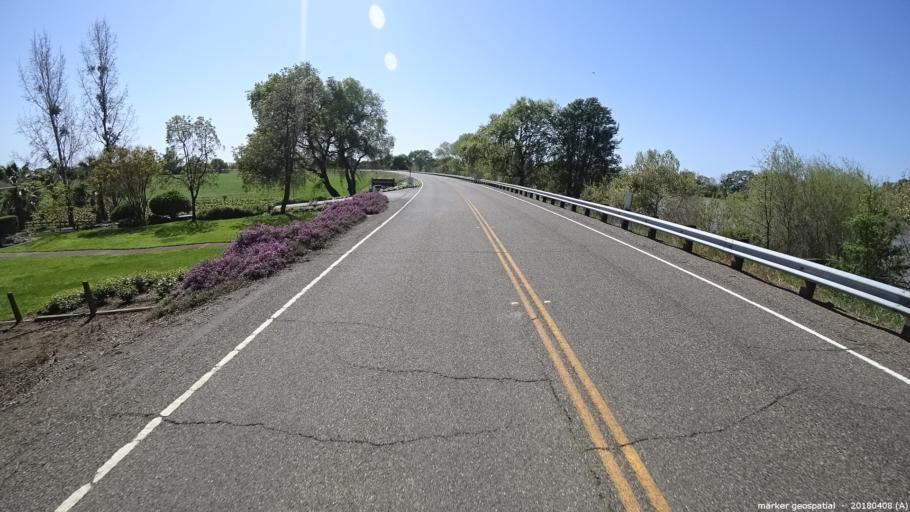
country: US
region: California
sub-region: Sacramento County
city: Parkway
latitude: 38.4337
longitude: -121.5280
